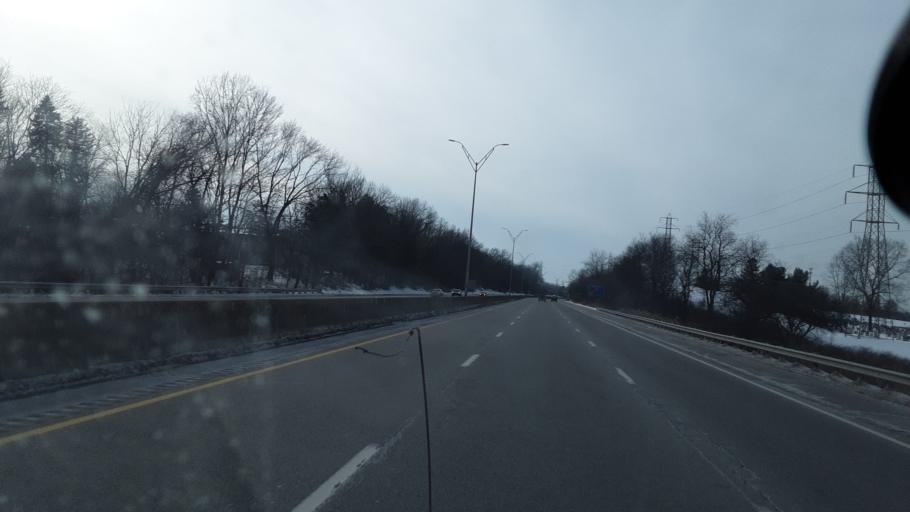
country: US
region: Ohio
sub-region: Summit County
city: Portage Lakes
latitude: 41.0248
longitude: -81.5182
